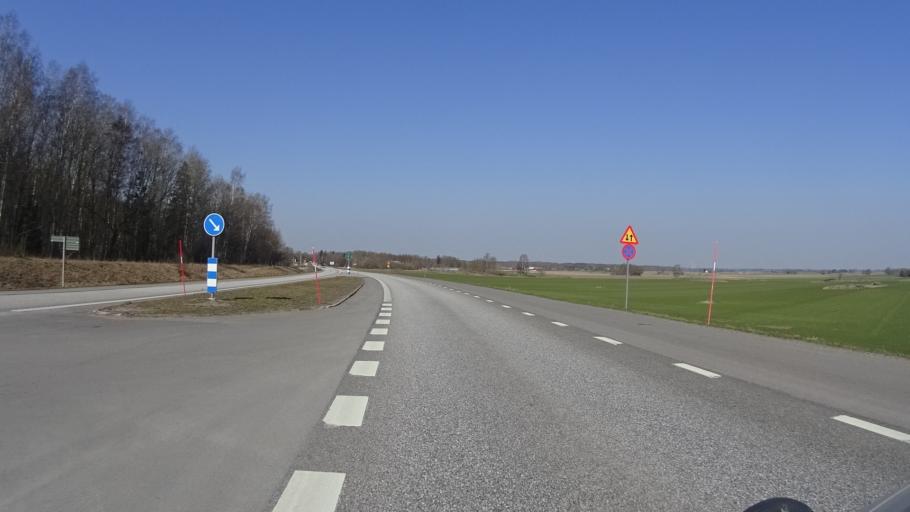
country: SE
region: OEstergoetland
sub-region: Mjolby Kommun
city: Mantorp
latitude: 58.3734
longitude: 15.2914
